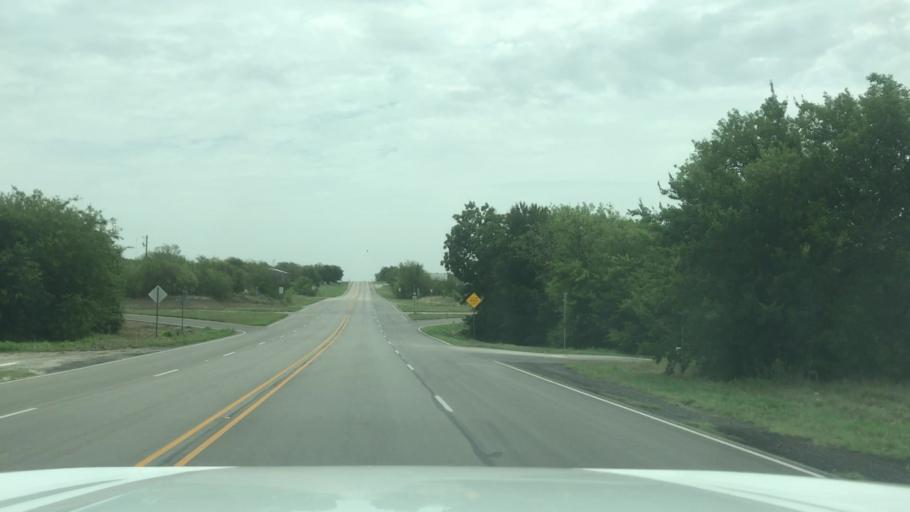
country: US
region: Texas
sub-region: Erath County
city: Dublin
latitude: 32.0591
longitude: -98.2077
